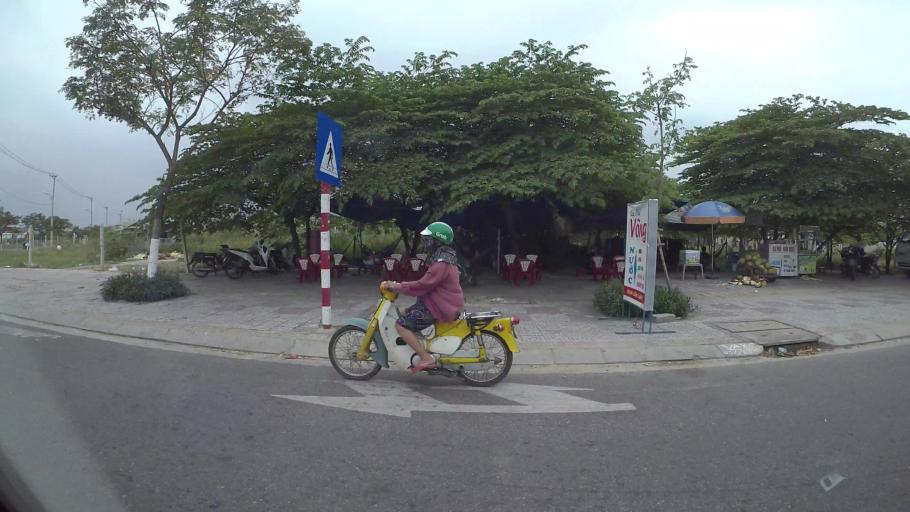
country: VN
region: Da Nang
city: Lien Chieu
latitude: 16.0676
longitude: 108.1701
